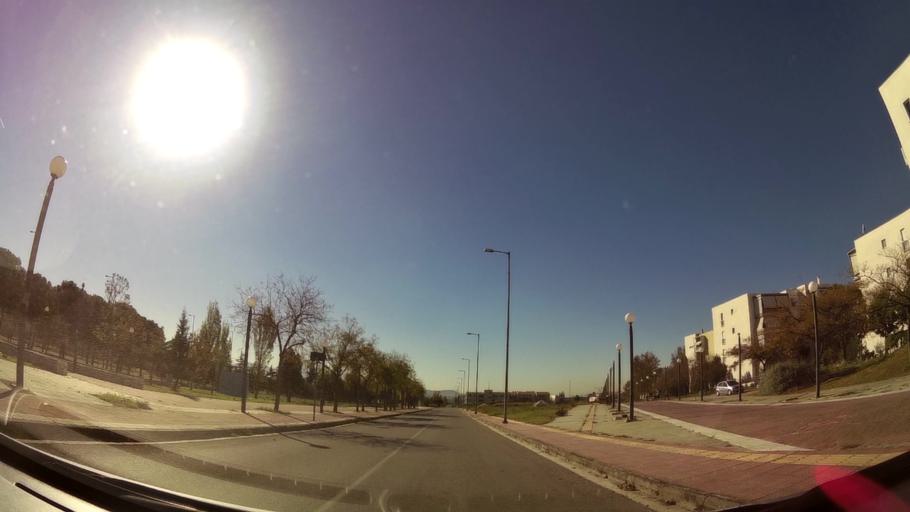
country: GR
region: Attica
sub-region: Nomarchia Anatolikis Attikis
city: Thrakomakedones
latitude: 38.1108
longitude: 23.7678
